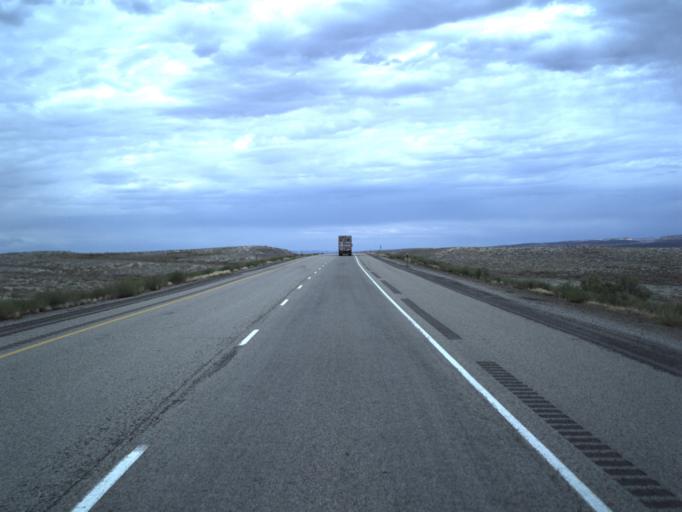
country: US
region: Utah
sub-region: Grand County
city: Moab
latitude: 38.9681
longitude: -109.3655
